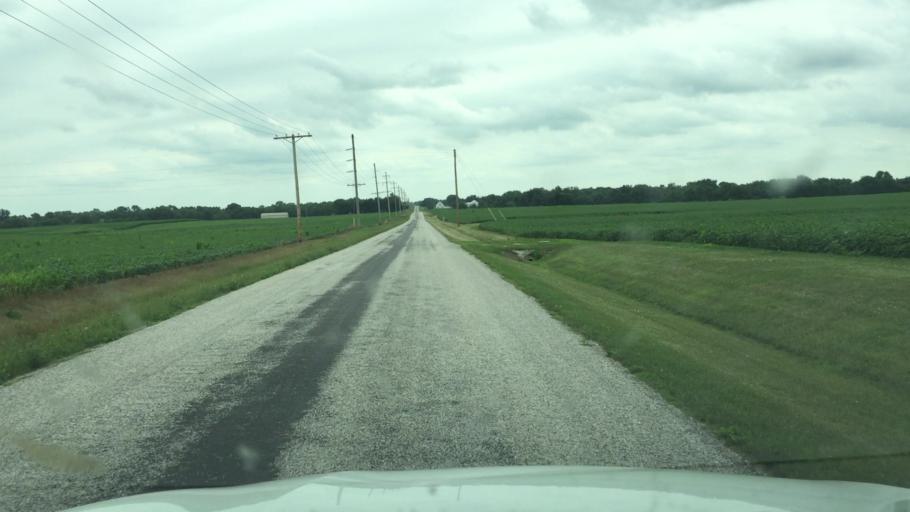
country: US
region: Illinois
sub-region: Hancock County
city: Carthage
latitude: 40.3085
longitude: -91.0829
